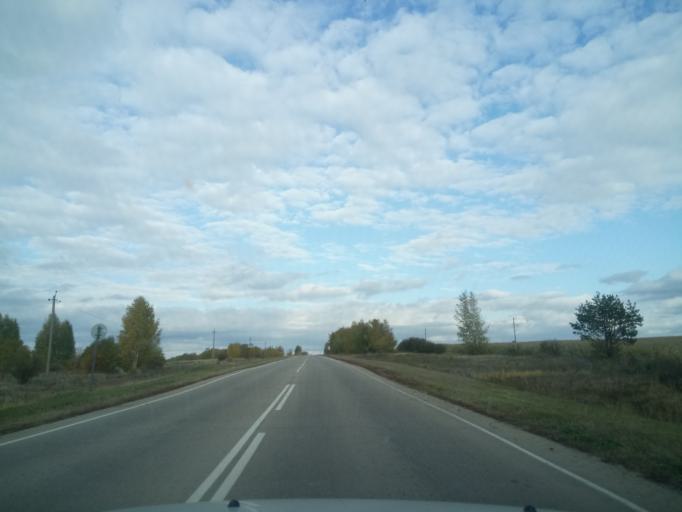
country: RU
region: Nizjnij Novgorod
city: Bol'shoye Boldino
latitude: 54.9654
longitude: 45.2440
